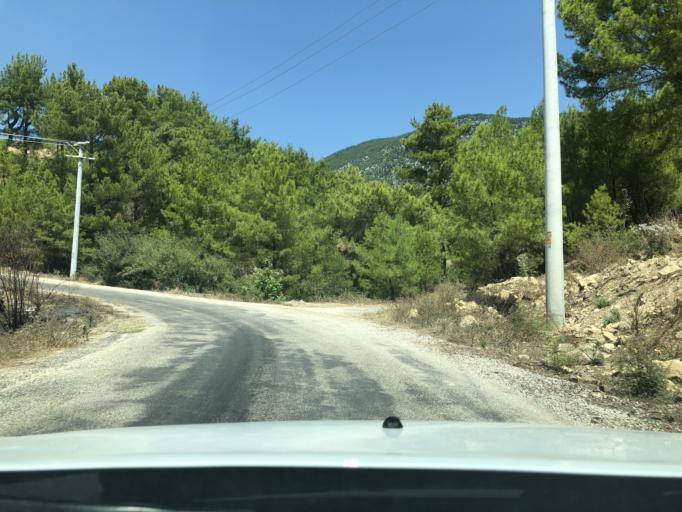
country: TR
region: Antalya
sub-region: Manavgat
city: Kizilagac
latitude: 36.8675
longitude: 31.5581
